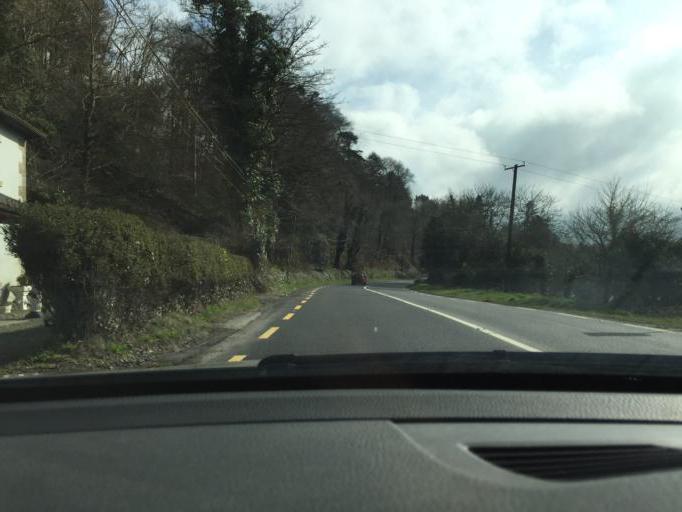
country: IE
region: Leinster
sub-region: South Dublin
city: Saggart
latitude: 53.2573
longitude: -6.4481
